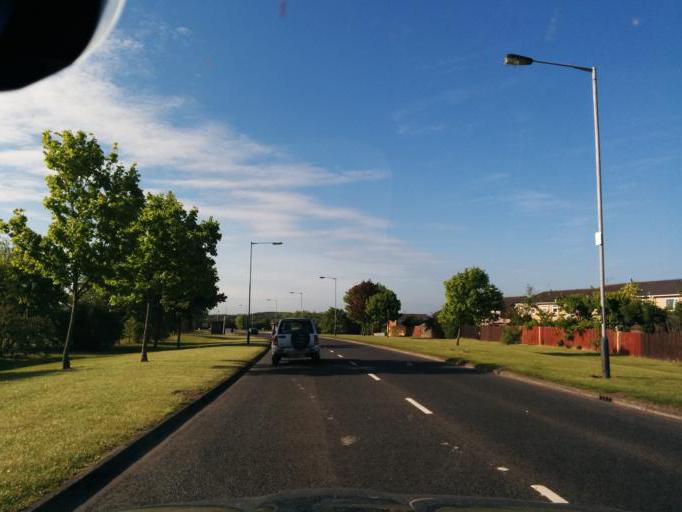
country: GB
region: England
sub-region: Northumberland
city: Cramlington
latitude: 55.0934
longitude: -1.5771
